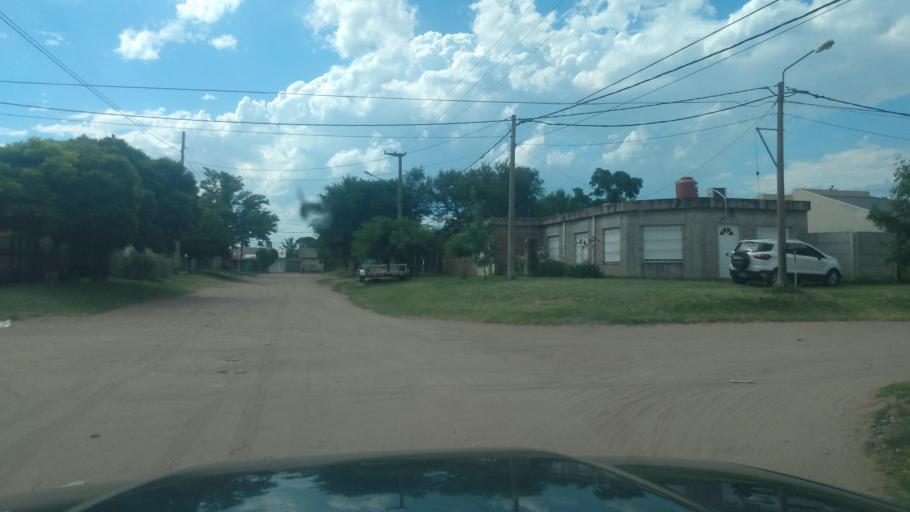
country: AR
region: La Pampa
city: Santa Rosa
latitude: -36.6442
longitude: -64.2848
